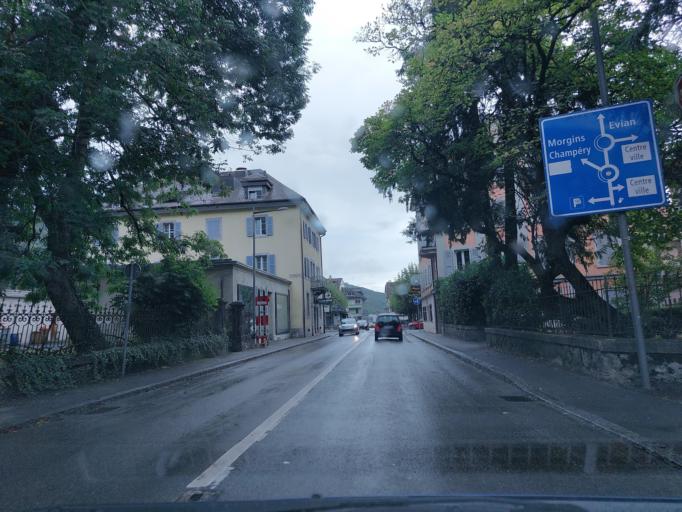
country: CH
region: Valais
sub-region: Monthey District
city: Monthey
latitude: 46.2508
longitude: 6.9475
